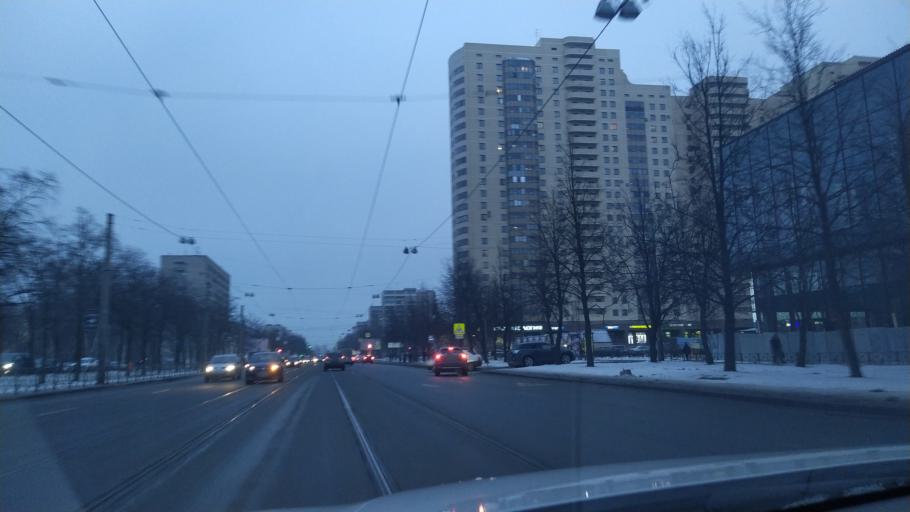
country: RU
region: Leningrad
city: Akademicheskoe
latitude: 60.0118
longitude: 30.4029
